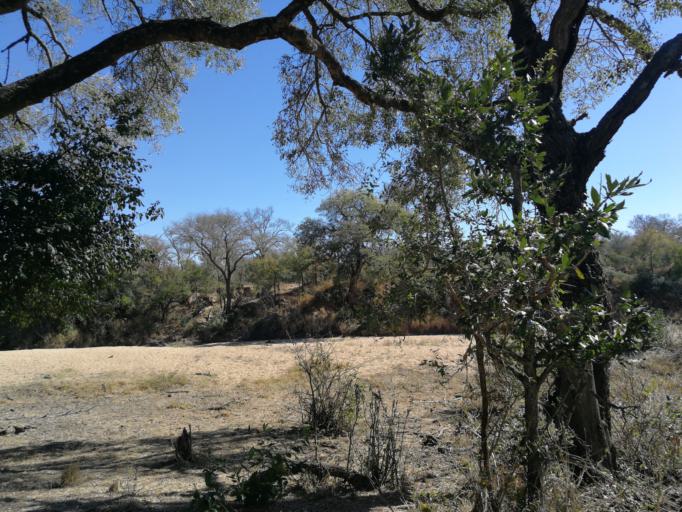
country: ZA
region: Limpopo
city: Thulamahashi
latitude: -24.9416
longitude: 31.6781
